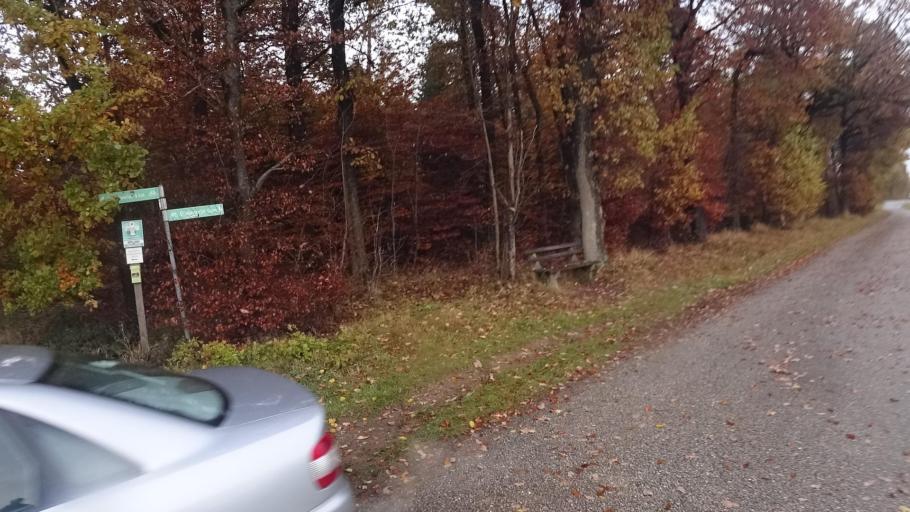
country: DE
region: Rheinland-Pfalz
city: Braunshorn
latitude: 50.0970
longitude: 7.5232
